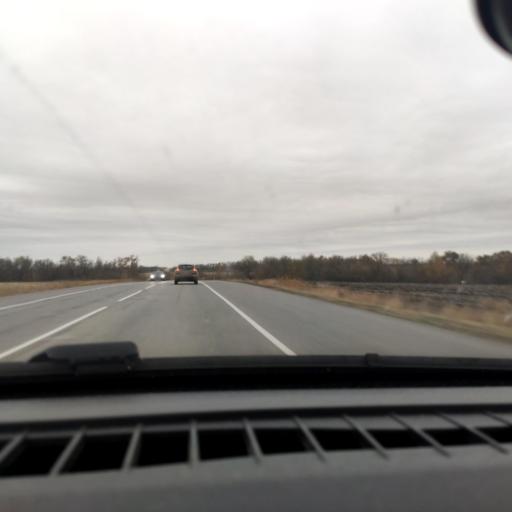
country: RU
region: Voronezj
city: Devitsa
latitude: 51.5818
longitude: 38.9759
